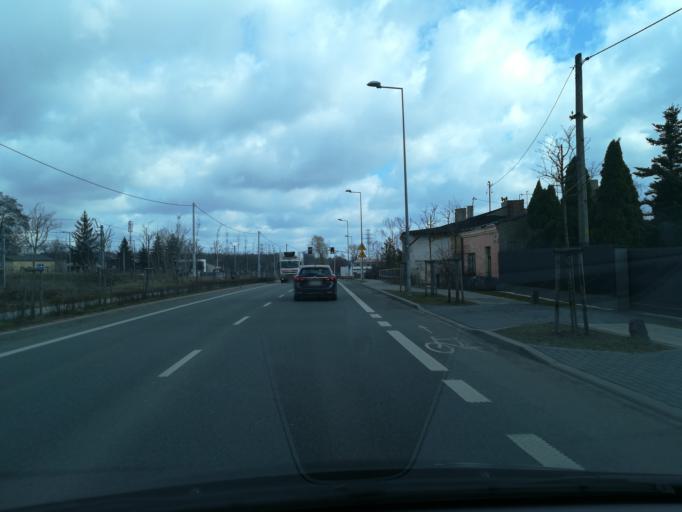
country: PL
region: Silesian Voivodeship
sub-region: Czestochowa
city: Czestochowa
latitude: 50.8280
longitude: 19.1372
